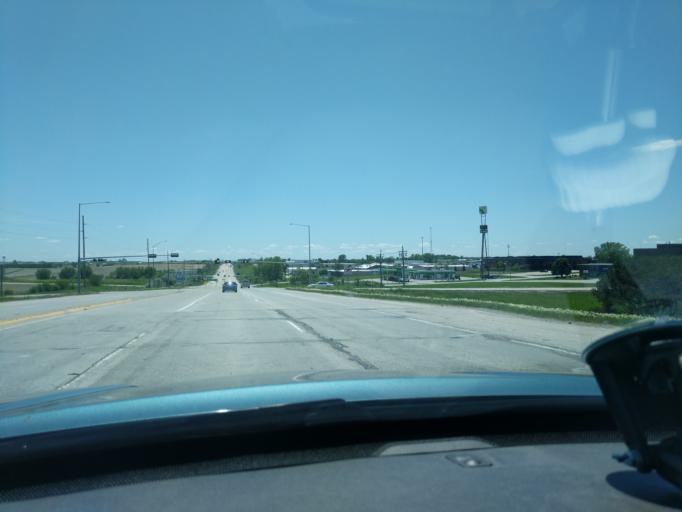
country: US
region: Nebraska
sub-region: Sarpy County
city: Chalco
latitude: 41.1610
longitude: -96.1389
